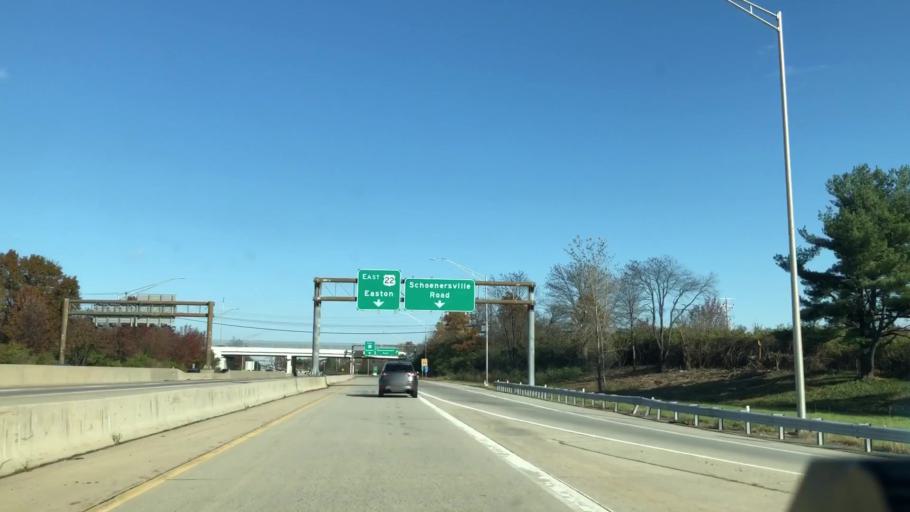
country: US
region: Pennsylvania
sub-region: Northampton County
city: Bethlehem
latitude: 40.6491
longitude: -75.4133
